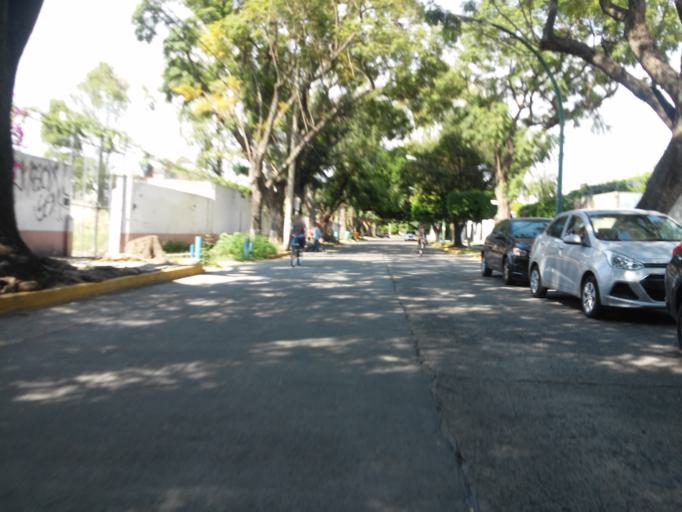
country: MX
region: Jalisco
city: Guadalajara
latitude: 20.6586
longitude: -103.3987
